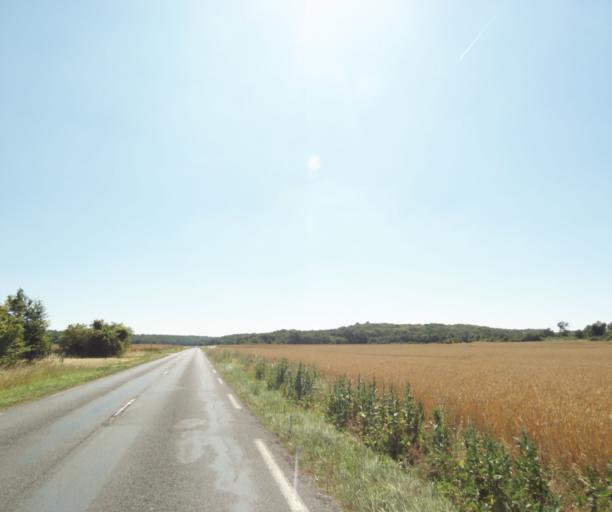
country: FR
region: Ile-de-France
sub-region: Departement de l'Essonne
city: Milly-la-Foret
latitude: 48.3769
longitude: 2.4751
